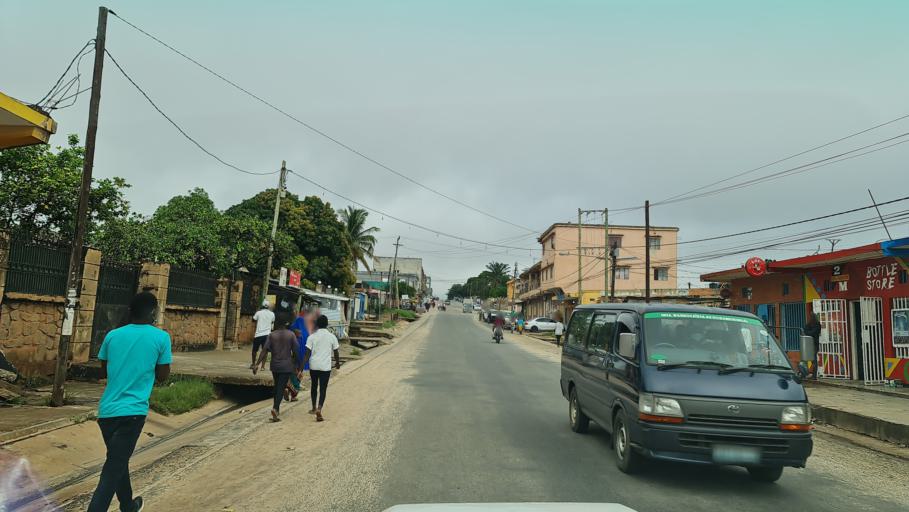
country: MZ
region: Nampula
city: Nampula
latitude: -15.1318
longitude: 39.2699
